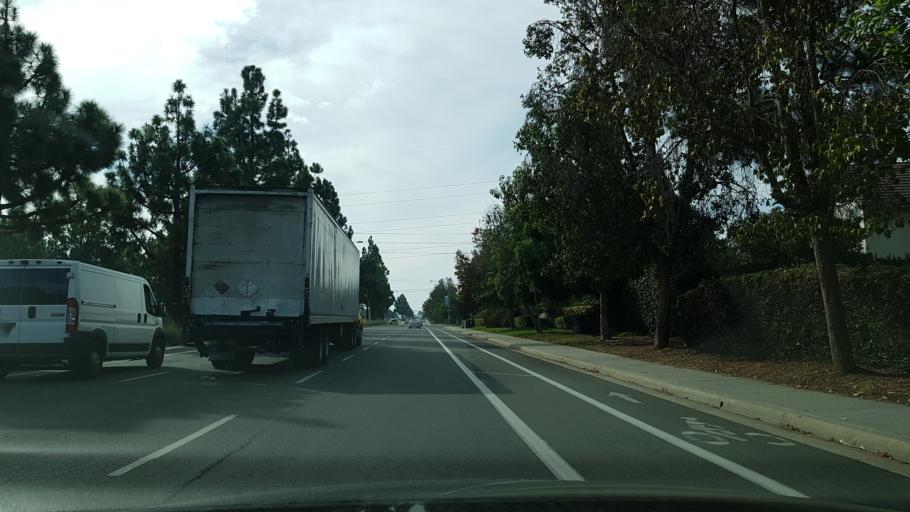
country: US
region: California
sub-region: San Diego County
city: Fairbanks Ranch
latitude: 32.9083
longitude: -117.1675
